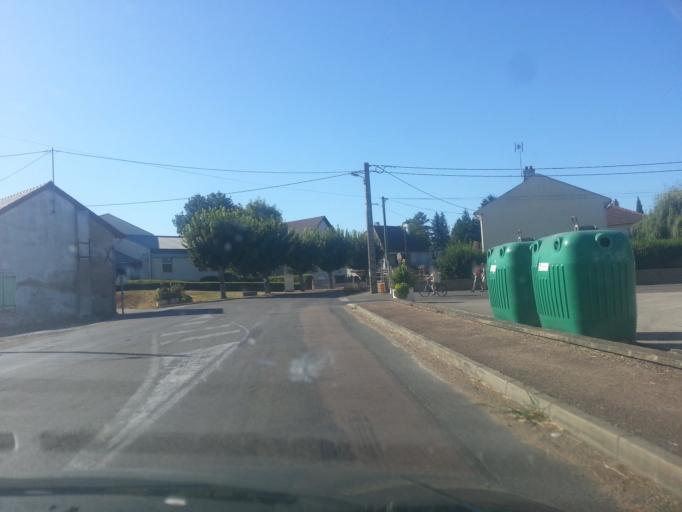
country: FR
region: Bourgogne
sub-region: Departement de Saone-et-Loire
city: Verdun-sur-le-Doubs
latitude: 46.8921
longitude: 5.0237
